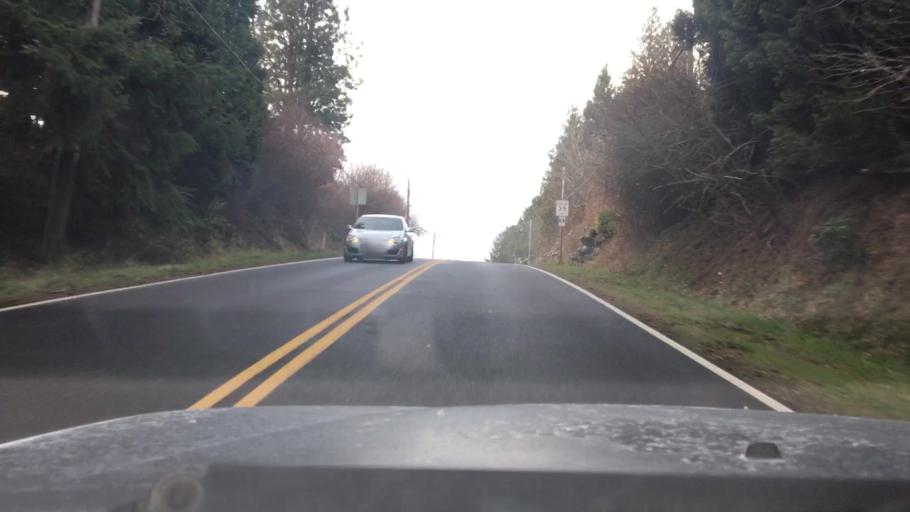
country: US
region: Washington
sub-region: Whatcom County
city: Ferndale
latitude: 48.8484
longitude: -122.6217
